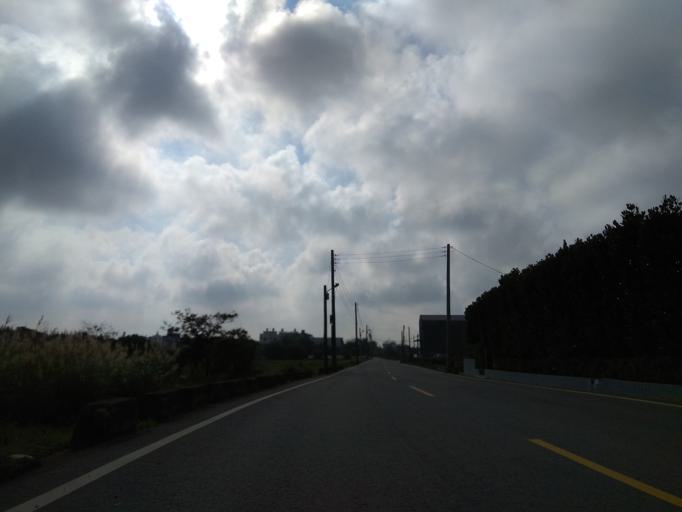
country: TW
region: Taiwan
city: Taoyuan City
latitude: 25.0555
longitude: 121.1493
